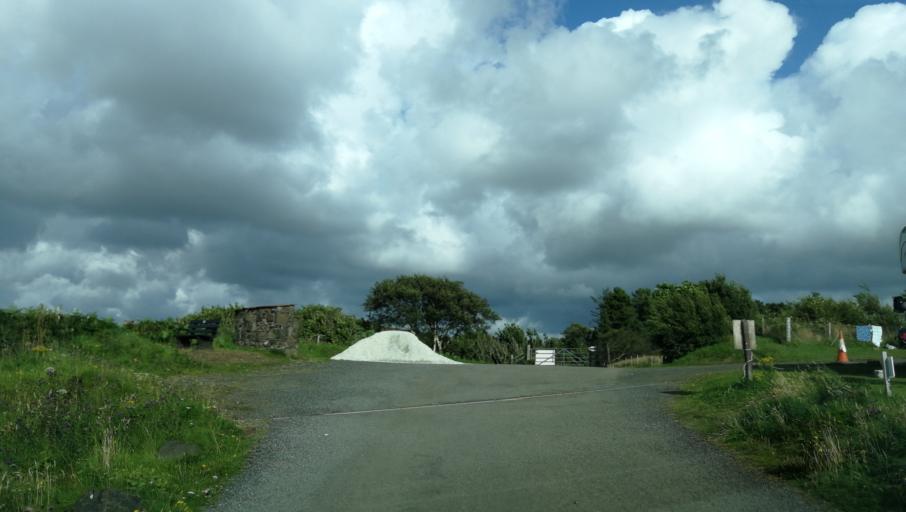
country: GB
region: Scotland
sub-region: Highland
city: Isle of Skye
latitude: 57.4317
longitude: -6.5790
